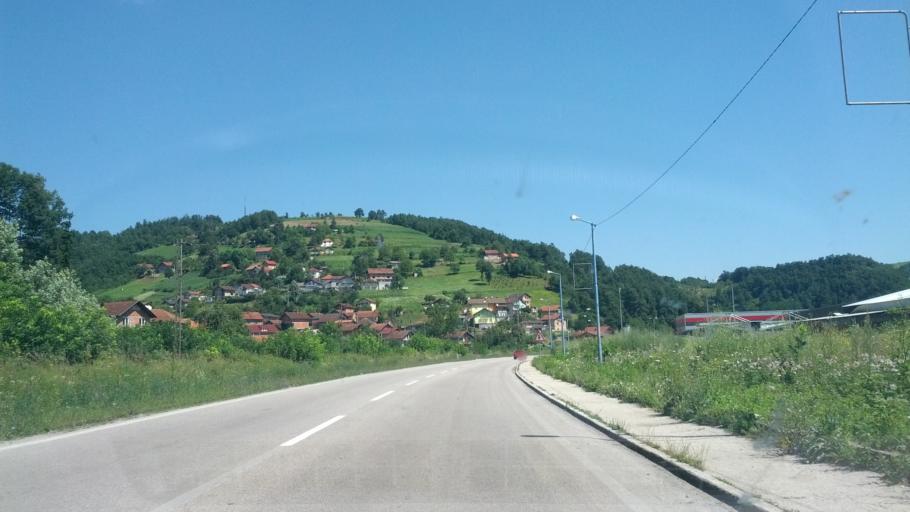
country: BA
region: Federation of Bosnia and Herzegovina
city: Bosanska Krupa
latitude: 44.8931
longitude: 16.1540
